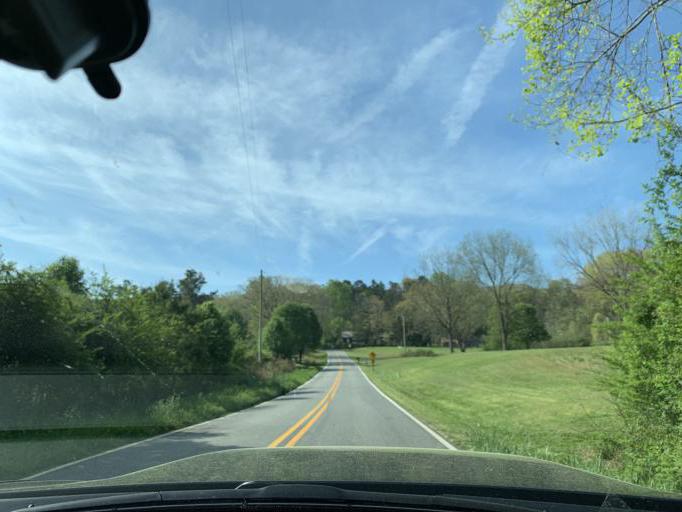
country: US
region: Georgia
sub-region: Forsyth County
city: Cumming
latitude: 34.2570
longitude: -84.1225
